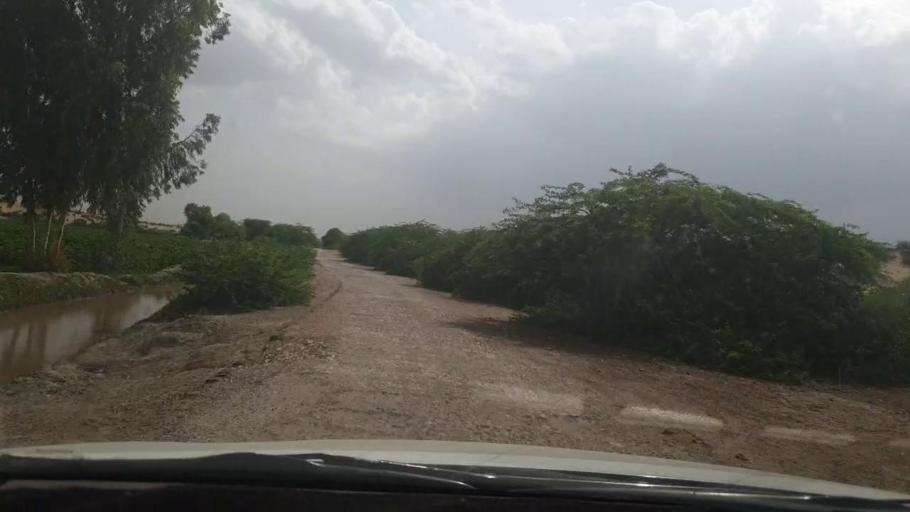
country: PK
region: Sindh
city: Kot Diji
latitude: 27.3439
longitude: 69.0211
